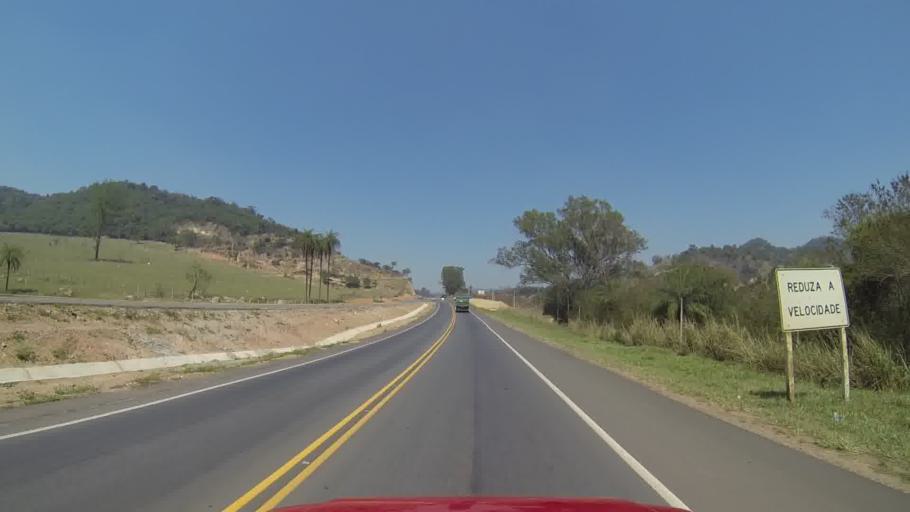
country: BR
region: Minas Gerais
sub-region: Mateus Leme
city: Mateus Leme
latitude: -20.0145
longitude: -44.4869
